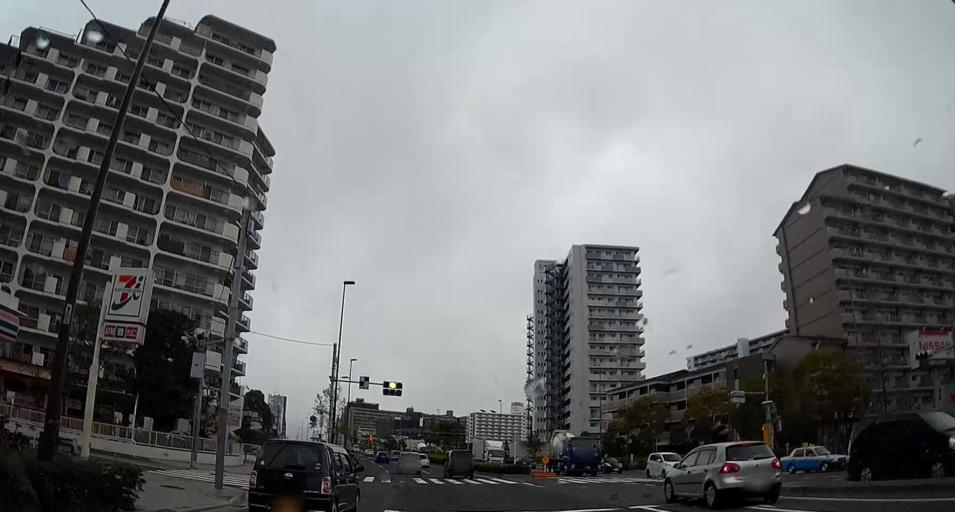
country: JP
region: Tokyo
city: Urayasu
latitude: 35.6976
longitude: 139.8433
